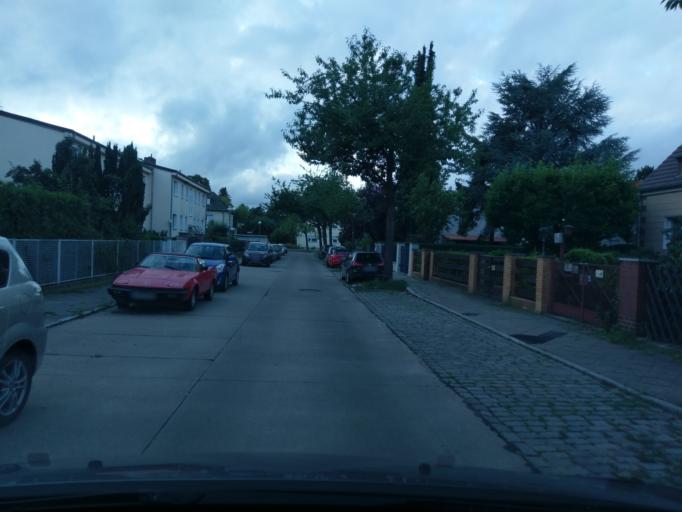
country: DE
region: Brandenburg
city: Teltow
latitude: 52.4218
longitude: 13.2775
